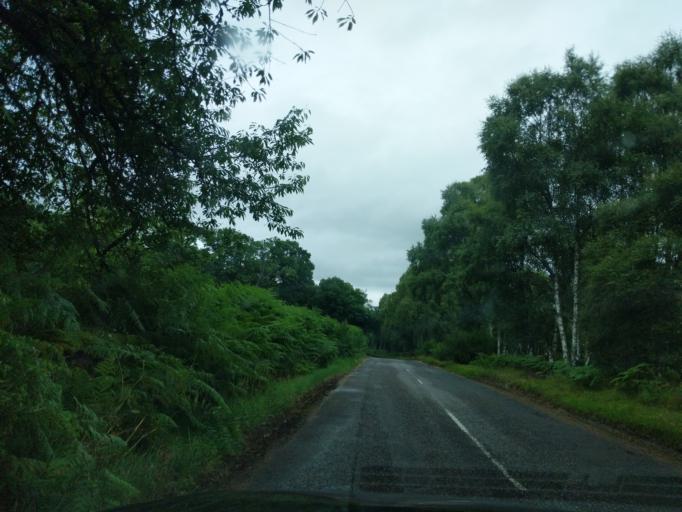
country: GB
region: Scotland
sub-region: Aberdeenshire
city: Ballater
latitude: 57.0746
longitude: -2.9444
